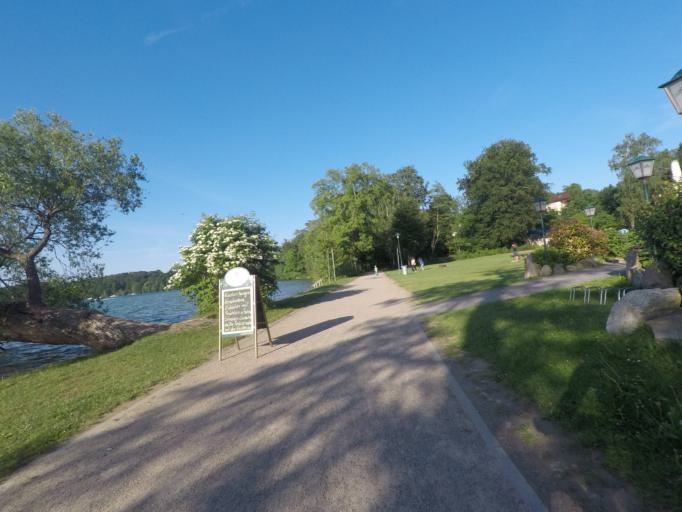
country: DE
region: Brandenburg
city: Joachimsthal
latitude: 52.9172
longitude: 13.7160
